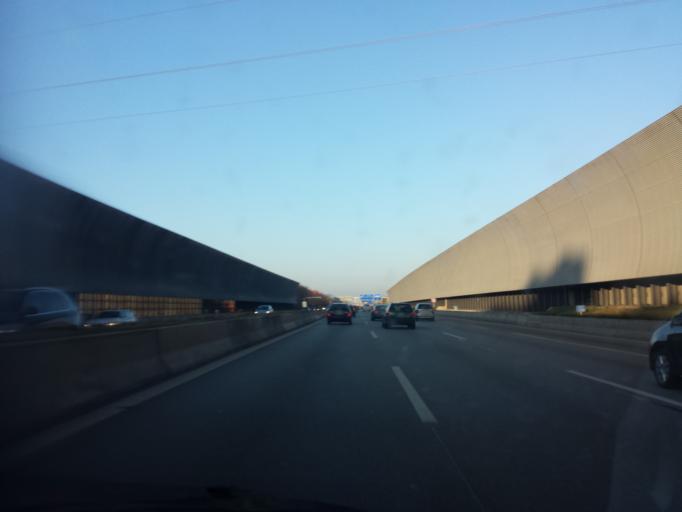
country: DE
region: Bavaria
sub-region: Upper Bavaria
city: Unterfoehring
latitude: 48.1977
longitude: 11.6176
